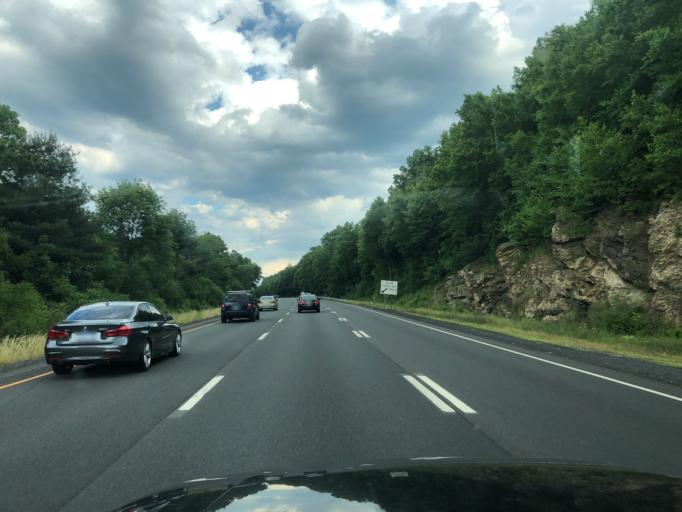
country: US
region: Connecticut
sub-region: Hartford County
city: Glastonbury Center
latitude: 41.6979
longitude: -72.5567
